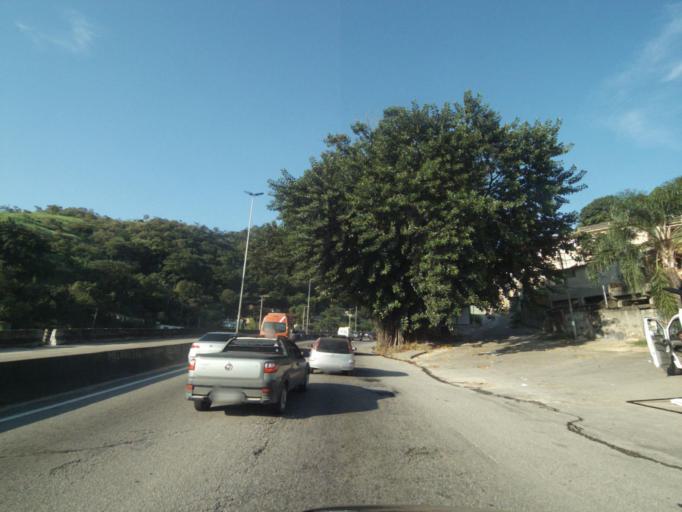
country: BR
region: Rio de Janeiro
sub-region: Niteroi
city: Niteroi
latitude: -22.8816
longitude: -43.0740
